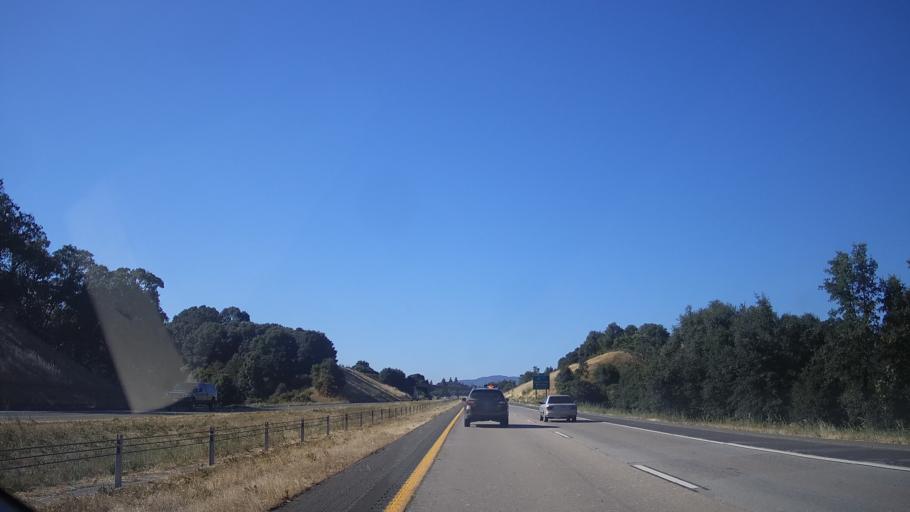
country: US
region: California
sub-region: Mendocino County
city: Redwood Valley
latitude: 39.2211
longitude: -123.2070
